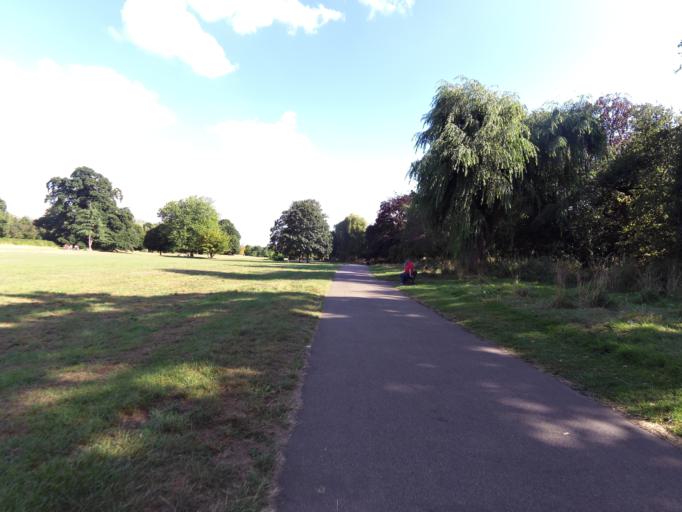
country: GB
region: England
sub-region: Greater London
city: Wood Green
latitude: 51.6202
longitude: -0.1345
